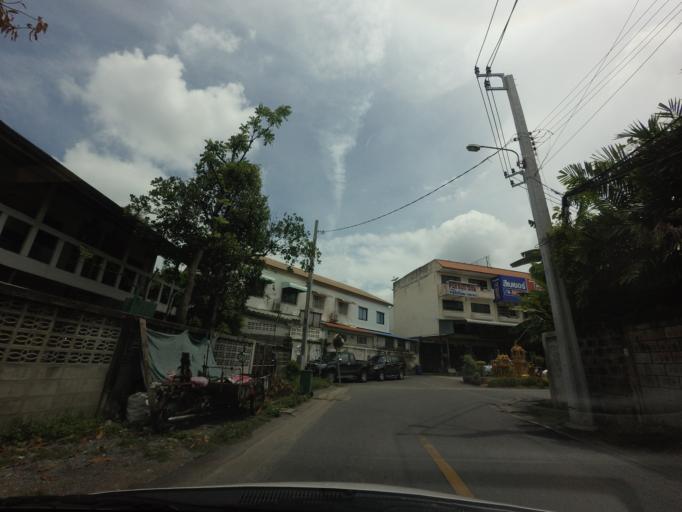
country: TH
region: Bangkok
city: Thung Khru
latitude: 13.6481
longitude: 100.5132
